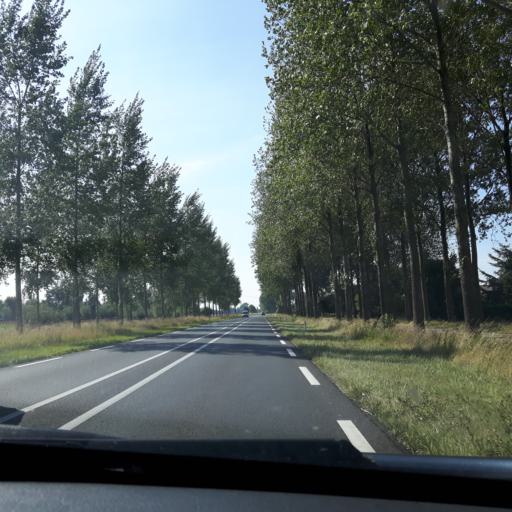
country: BE
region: Flanders
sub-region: Provincie Oost-Vlaanderen
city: Sint-Laureins
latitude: 51.3386
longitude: 3.5190
